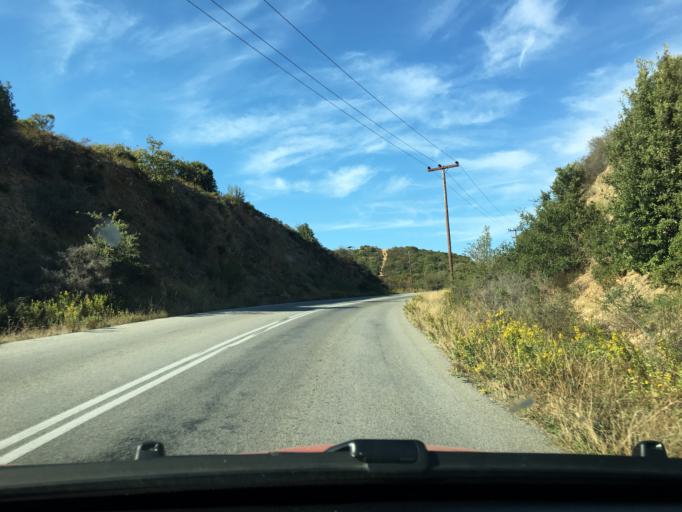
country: GR
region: Central Macedonia
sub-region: Nomos Chalkidikis
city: Ierissos
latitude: 40.3796
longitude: 23.8323
